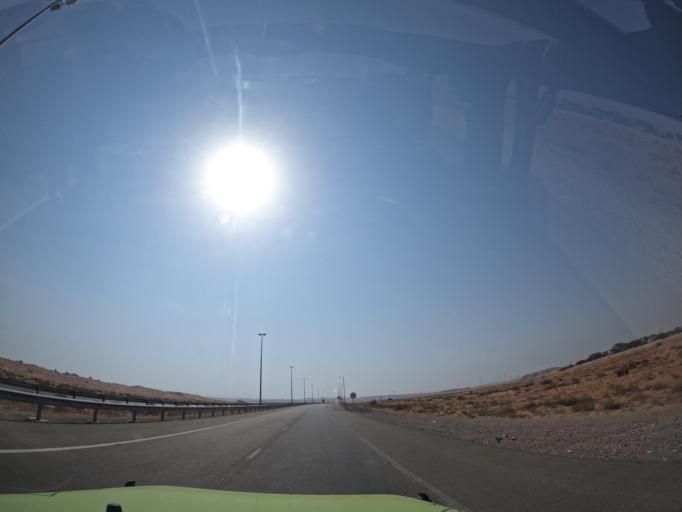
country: OM
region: Al Buraimi
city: Al Buraymi
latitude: 24.3987
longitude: 55.7165
